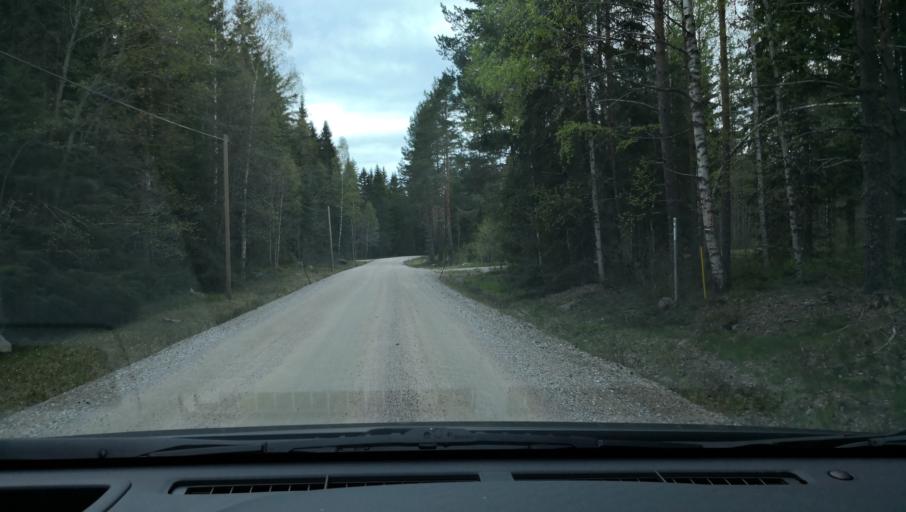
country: SE
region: Vaestmanland
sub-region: Fagersta Kommun
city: Fagersta
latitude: 60.0911
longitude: 15.8019
